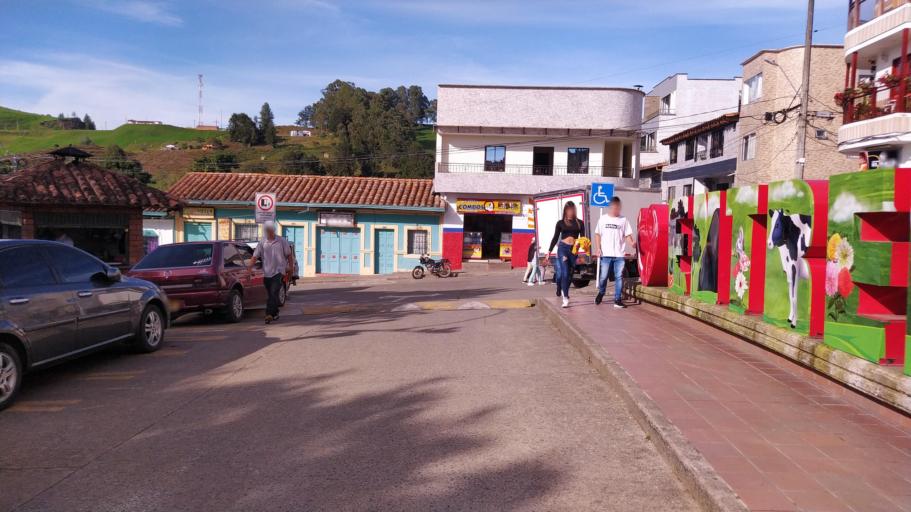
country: CO
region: Antioquia
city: Entrerrios
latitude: 6.5672
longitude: -75.5170
